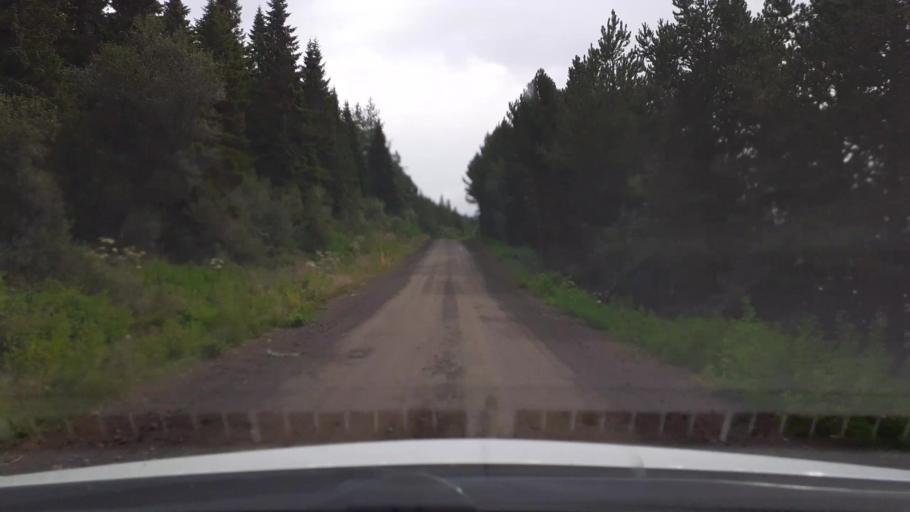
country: IS
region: Capital Region
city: Mosfellsbaer
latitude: 64.5179
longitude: -21.4247
